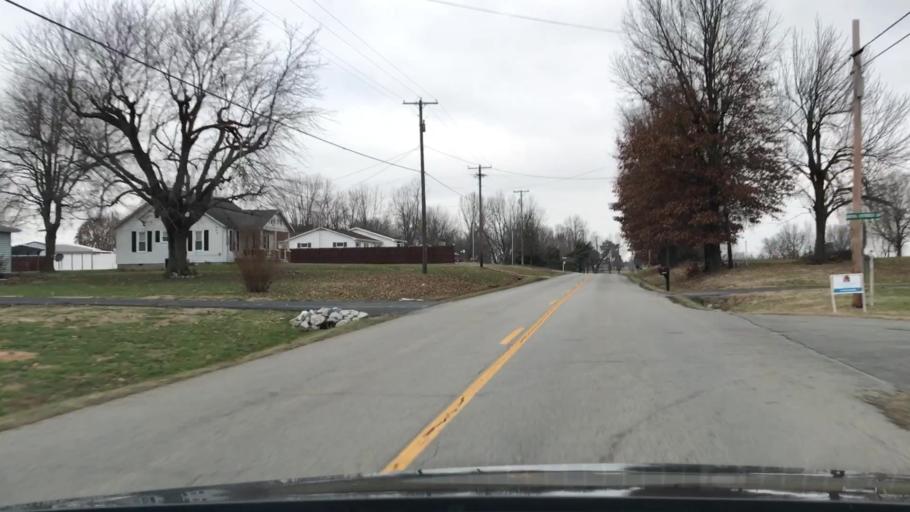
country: US
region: Kentucky
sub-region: Muhlenberg County
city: Morehead
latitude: 37.3896
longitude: -87.2538
